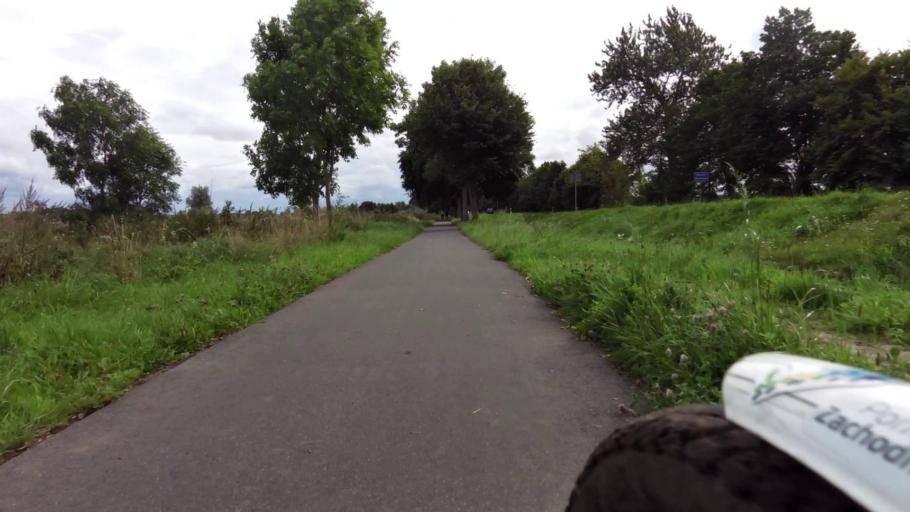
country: PL
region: West Pomeranian Voivodeship
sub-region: Powiat koszalinski
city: Mielno
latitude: 54.2448
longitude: 16.0654
